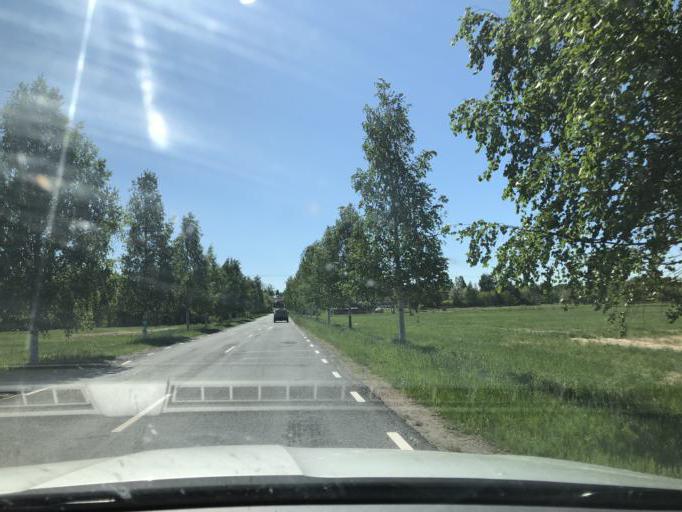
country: SE
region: Norrbotten
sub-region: Lulea Kommun
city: Gammelstad
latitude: 65.6501
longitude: 22.0196
